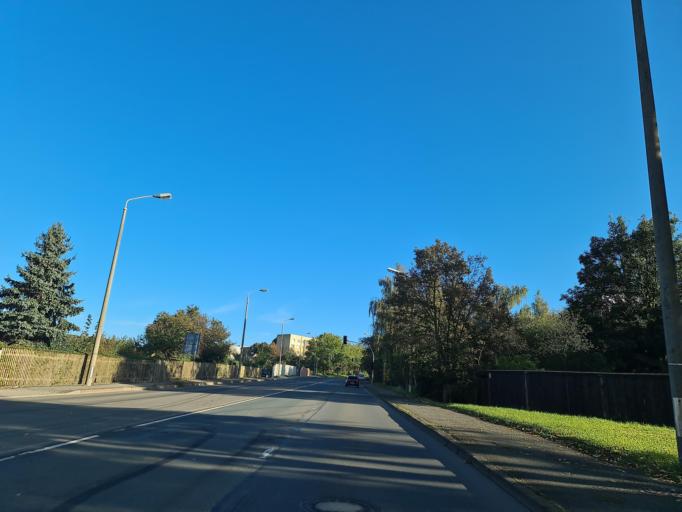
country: DE
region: Thuringia
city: Gera
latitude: 50.8917
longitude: 12.0869
